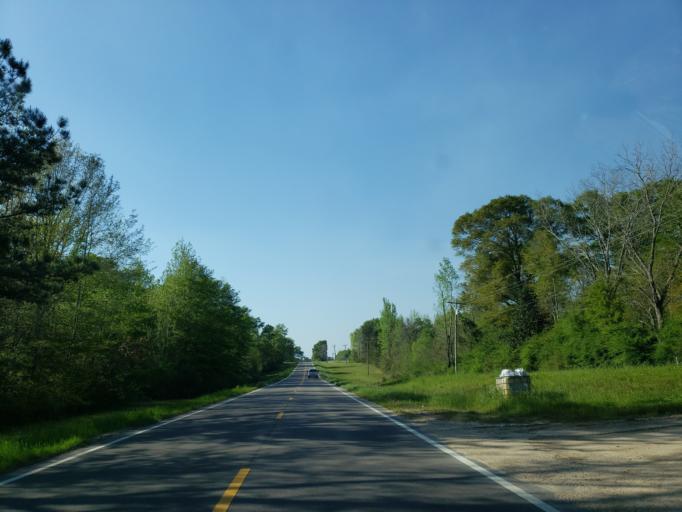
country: US
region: Mississippi
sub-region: Perry County
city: Richton
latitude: 31.4235
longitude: -88.9604
